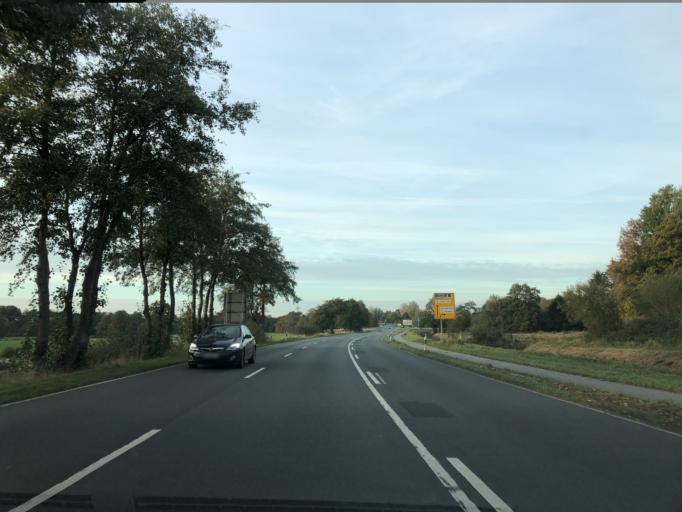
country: DE
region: Lower Saxony
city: Papenburg
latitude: 53.0771
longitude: 7.3805
